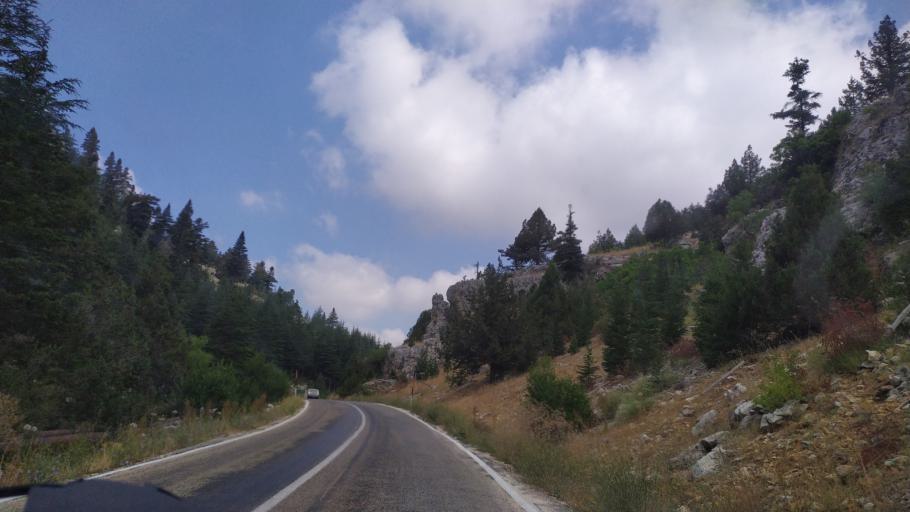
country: TR
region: Mersin
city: Kirobasi
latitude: 36.6117
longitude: 33.8806
